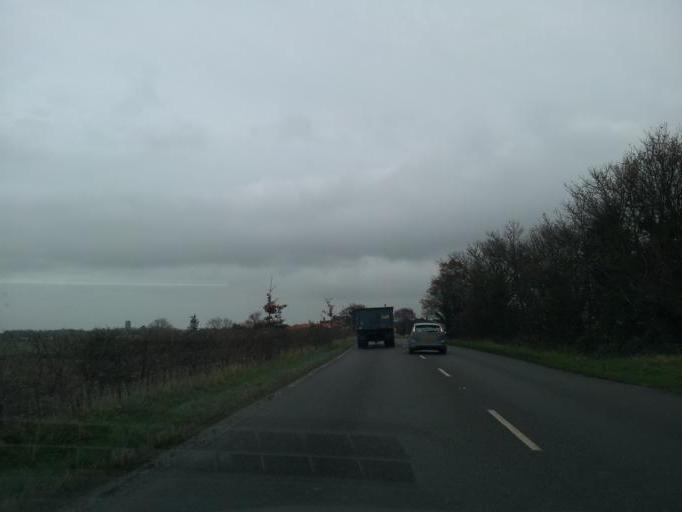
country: GB
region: England
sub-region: Norfolk
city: Martham
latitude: 52.6989
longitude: 1.6165
